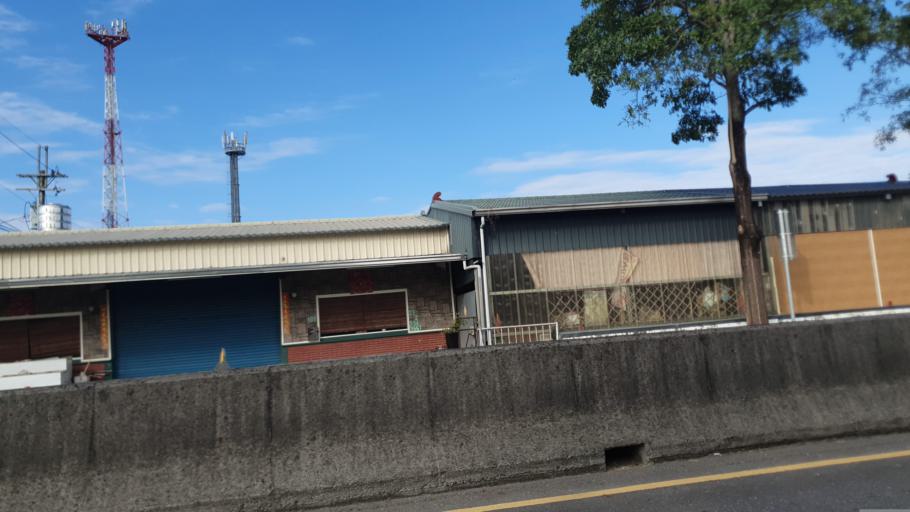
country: TW
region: Taiwan
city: Yujing
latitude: 23.0535
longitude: 120.4111
